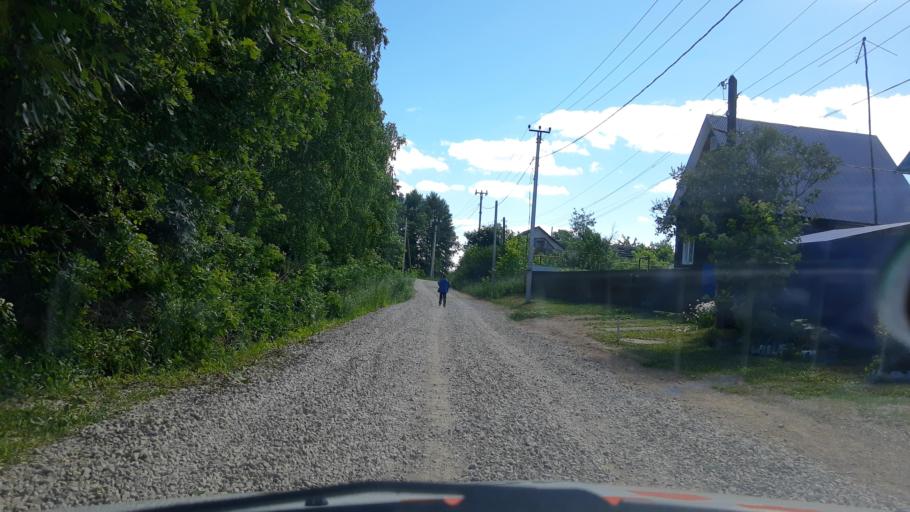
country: RU
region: Bashkortostan
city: Iglino
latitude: 54.8424
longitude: 56.4228
